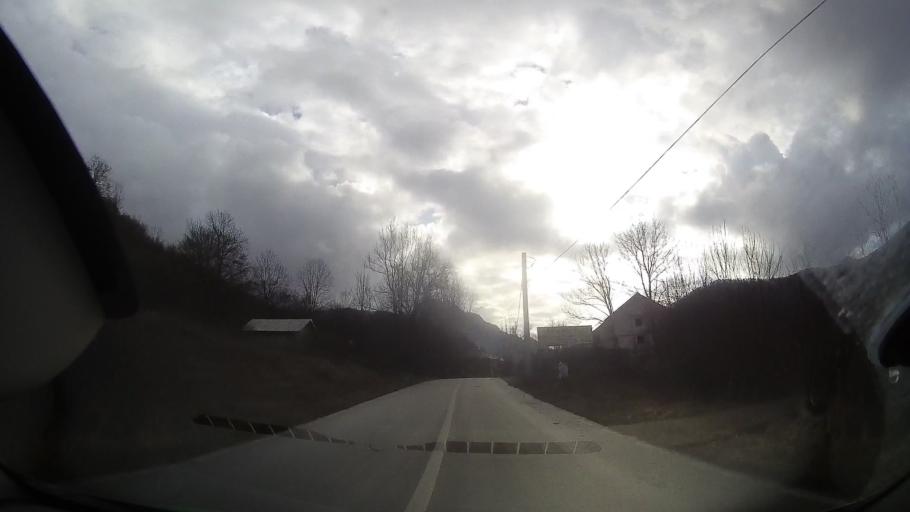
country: RO
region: Alba
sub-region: Comuna Rimetea
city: Rimetea
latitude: 46.4852
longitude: 23.5810
